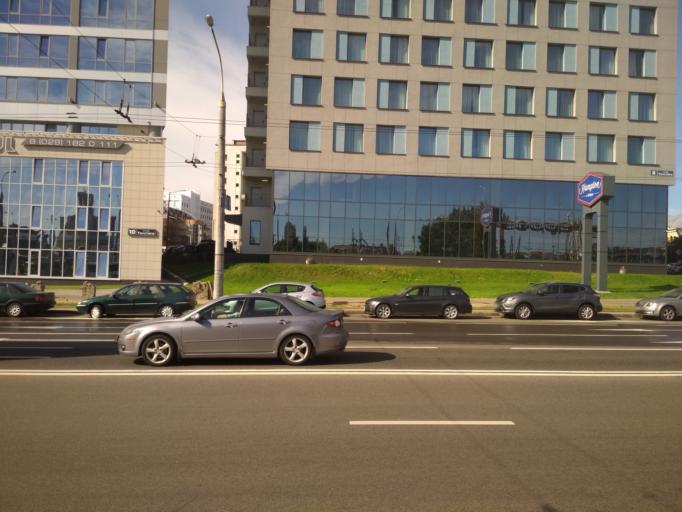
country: BY
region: Minsk
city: Minsk
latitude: 53.8890
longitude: 27.5447
